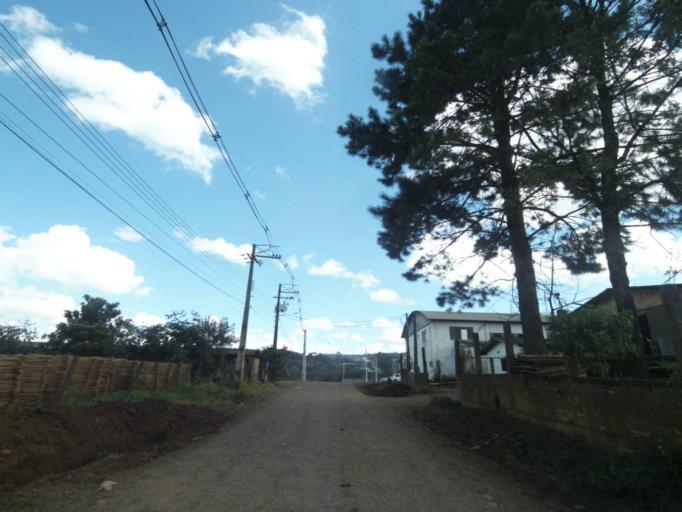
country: BR
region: Parana
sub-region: Uniao Da Vitoria
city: Uniao da Vitoria
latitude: -26.1524
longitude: -51.5385
